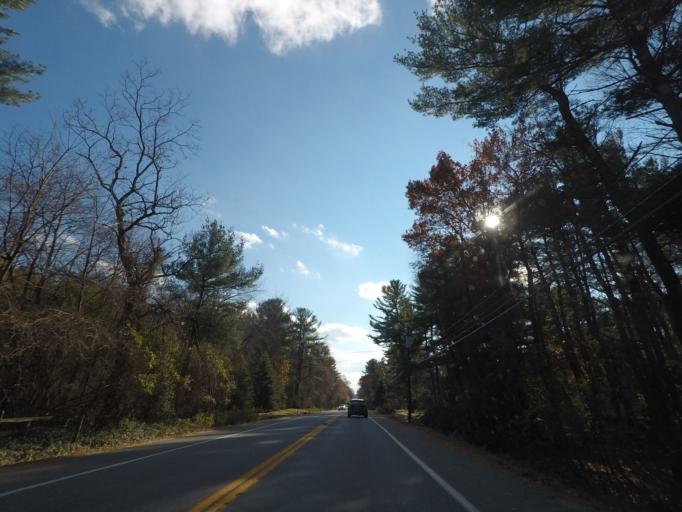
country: US
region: New York
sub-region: Schenectady County
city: East Glenville
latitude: 42.8724
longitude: -73.8877
